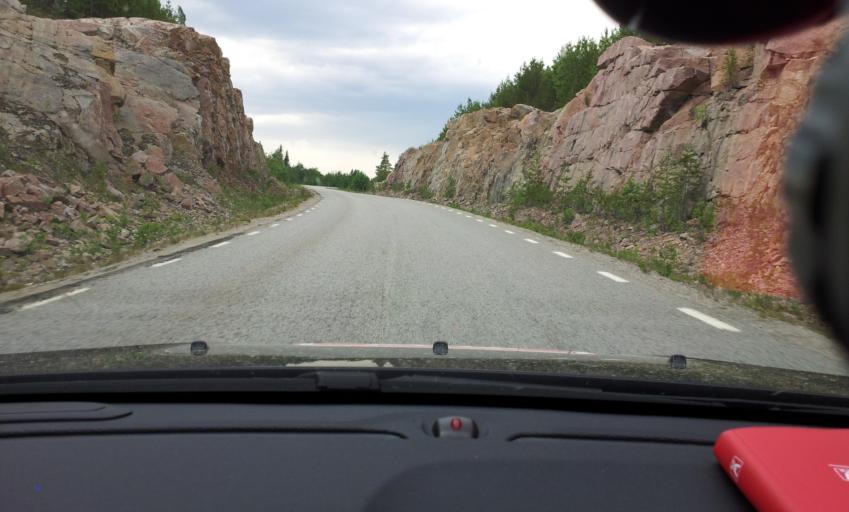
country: SE
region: Jaemtland
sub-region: Bergs Kommun
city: Hoverberg
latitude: 62.6769
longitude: 14.7071
